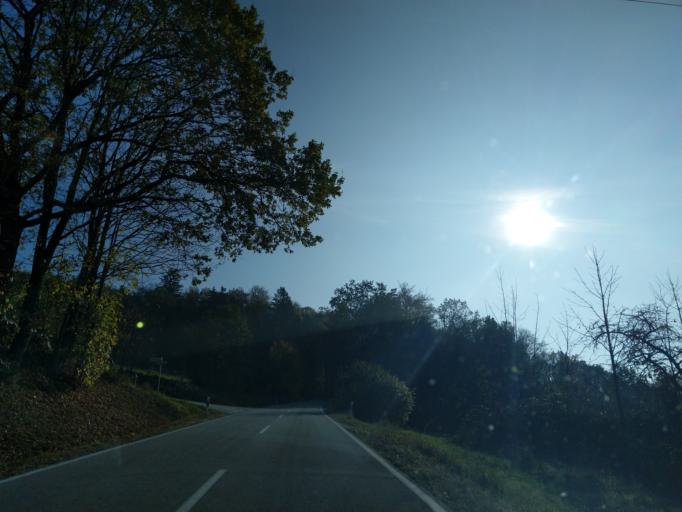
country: DE
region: Bavaria
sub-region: Lower Bavaria
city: Lalling
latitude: 48.8566
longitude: 13.1420
